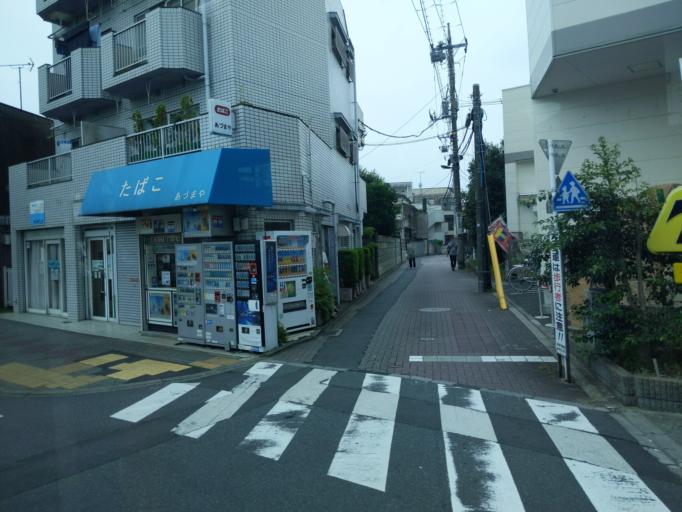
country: JP
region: Saitama
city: Wako
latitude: 35.7733
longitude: 139.6464
